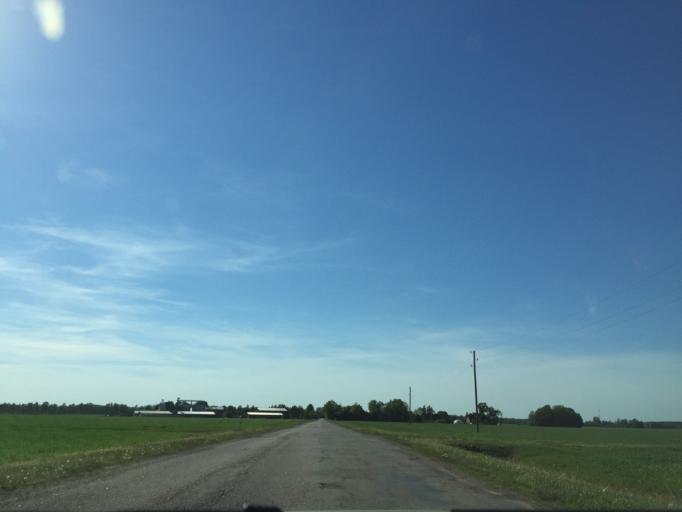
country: LV
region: Jelgava
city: Jelgava
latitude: 56.5225
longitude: 23.7272
